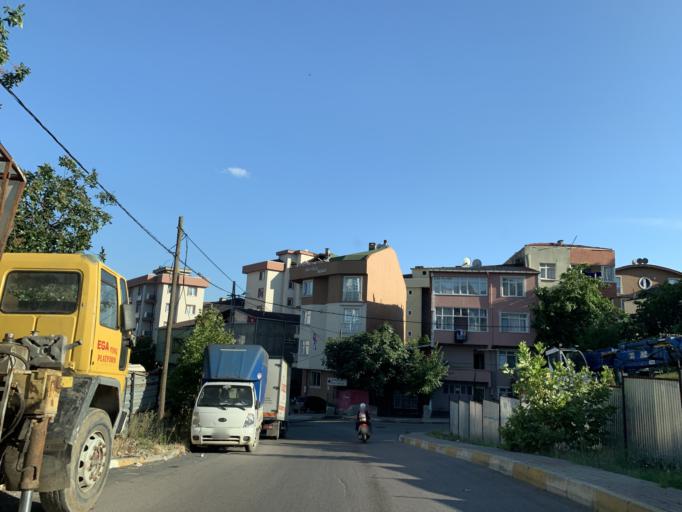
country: TR
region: Istanbul
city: Pendik
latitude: 40.8980
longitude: 29.2580
